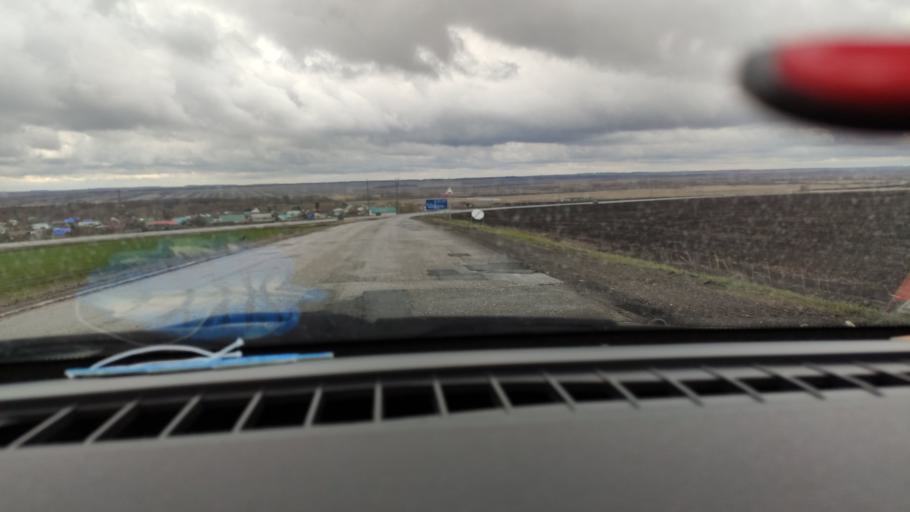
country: RU
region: Tatarstan
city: Nurlat
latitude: 54.3982
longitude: 50.7821
